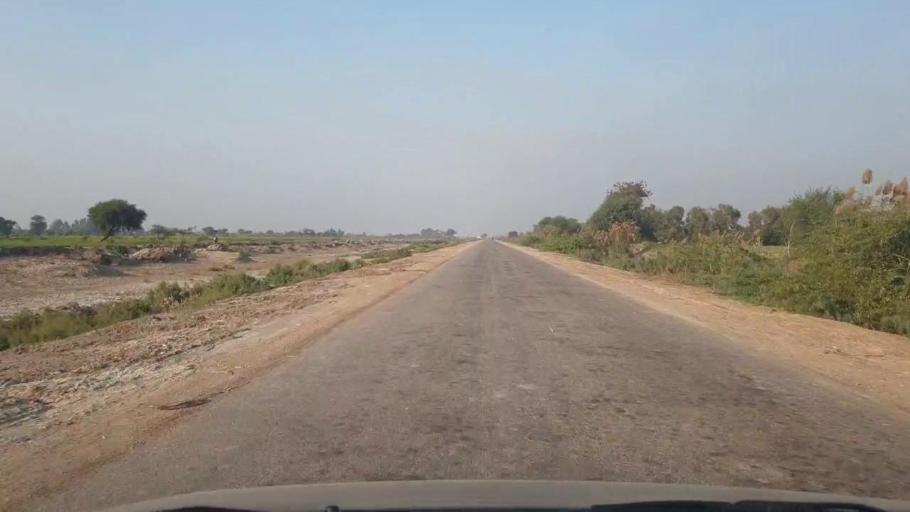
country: PK
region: Sindh
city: Mirwah Gorchani
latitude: 25.3386
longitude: 69.1689
